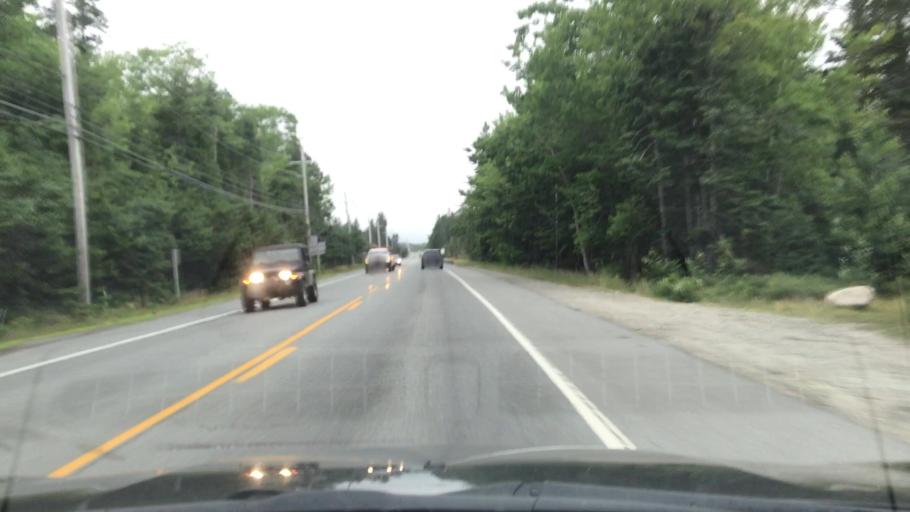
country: US
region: Maine
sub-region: Hancock County
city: Trenton
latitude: 44.4233
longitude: -68.3646
